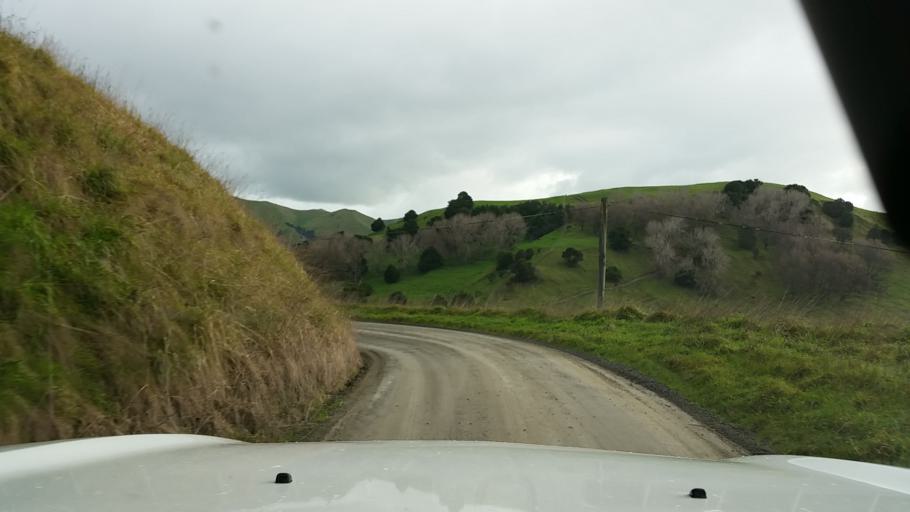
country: NZ
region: Wellington
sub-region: South Wairarapa District
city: Waipawa
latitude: -41.2158
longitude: 175.5863
